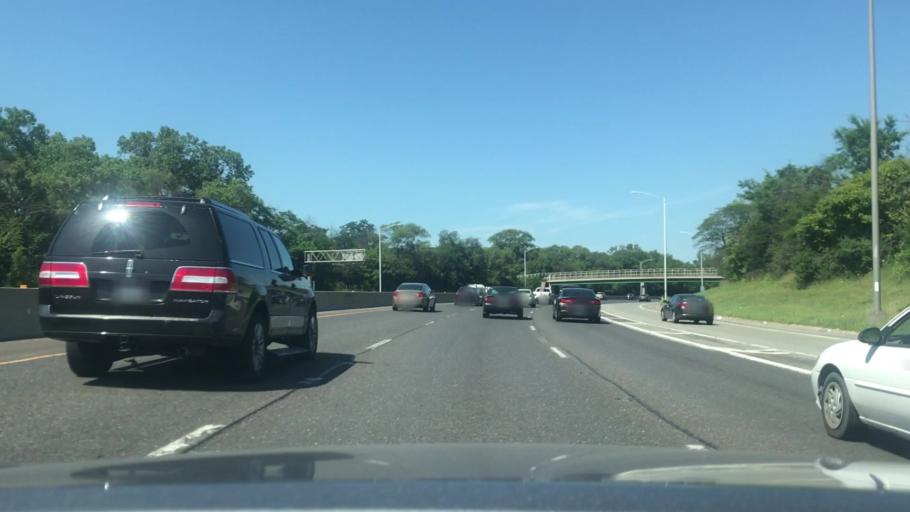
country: US
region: Illinois
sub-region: Cook County
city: Calumet Park
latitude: 41.6954
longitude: -87.6589
